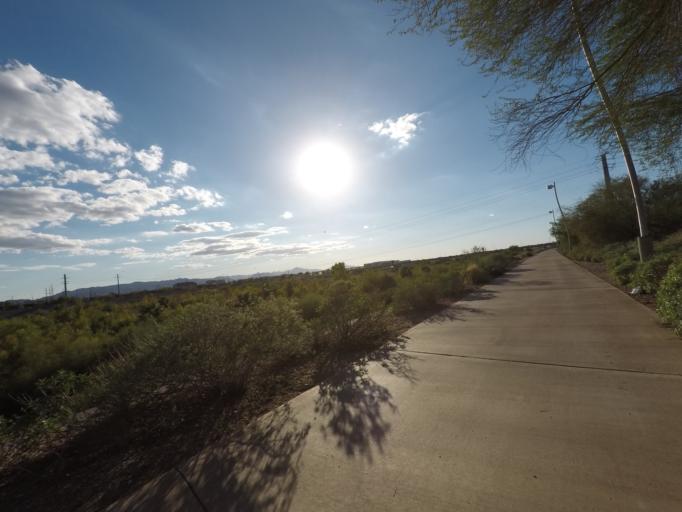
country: US
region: Arizona
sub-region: Maricopa County
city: Tempe Junction
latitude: 33.4359
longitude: -111.9551
